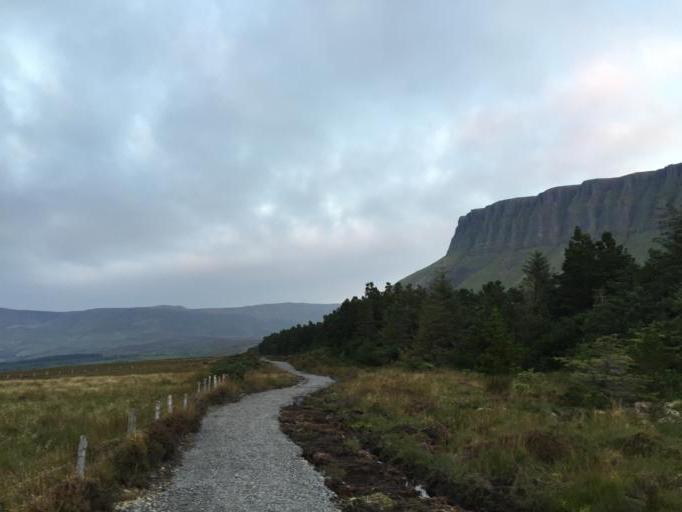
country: IE
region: Connaught
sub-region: Sligo
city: Sligo
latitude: 54.3709
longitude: -8.4938
